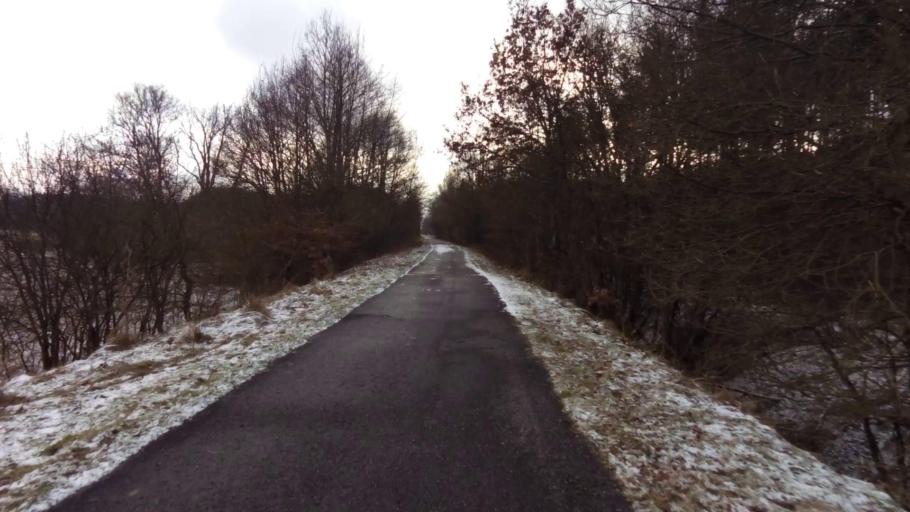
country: PL
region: West Pomeranian Voivodeship
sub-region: Powiat drawski
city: Zlocieniec
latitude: 53.5797
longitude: 16.0400
